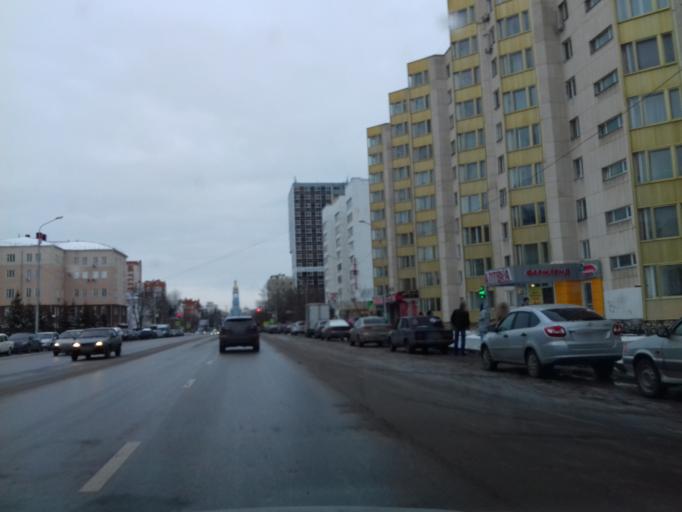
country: RU
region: Bashkortostan
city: Ufa
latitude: 54.7286
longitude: 55.9650
